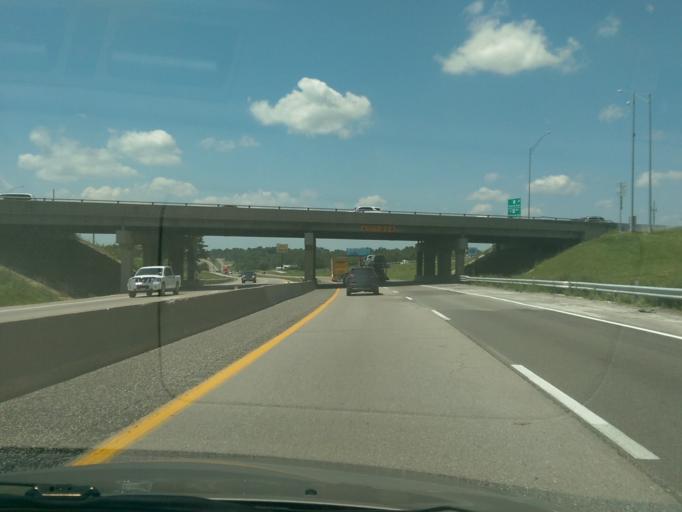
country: US
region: Missouri
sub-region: Boone County
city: Columbia
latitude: 38.9680
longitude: -92.3703
